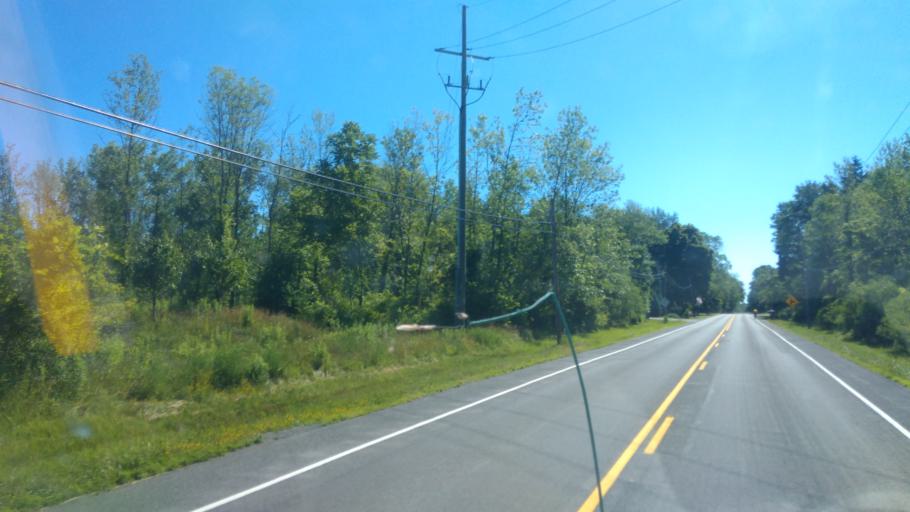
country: US
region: New York
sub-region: Monroe County
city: Webster
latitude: 43.2693
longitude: -77.3907
